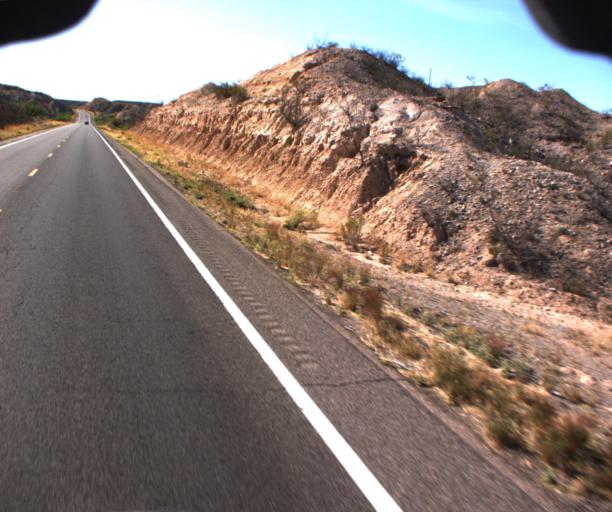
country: US
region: Arizona
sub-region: Cochise County
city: Saint David
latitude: 31.8269
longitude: -110.1778
